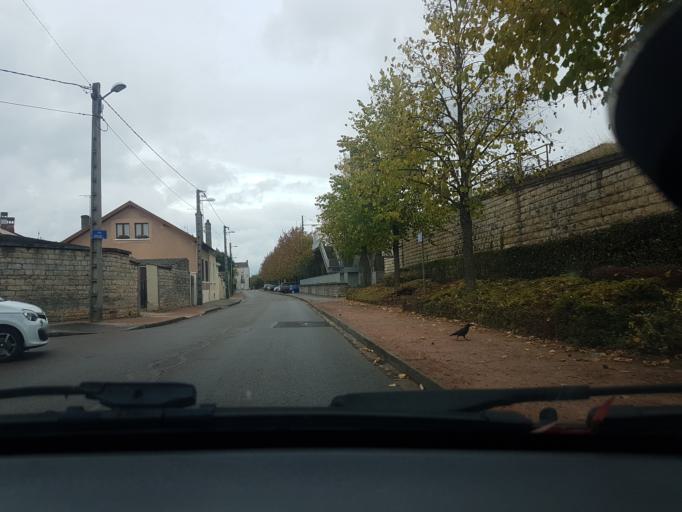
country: FR
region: Bourgogne
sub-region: Departement de la Cote-d'Or
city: Saint-Apollinaire
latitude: 47.3233
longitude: 5.0557
